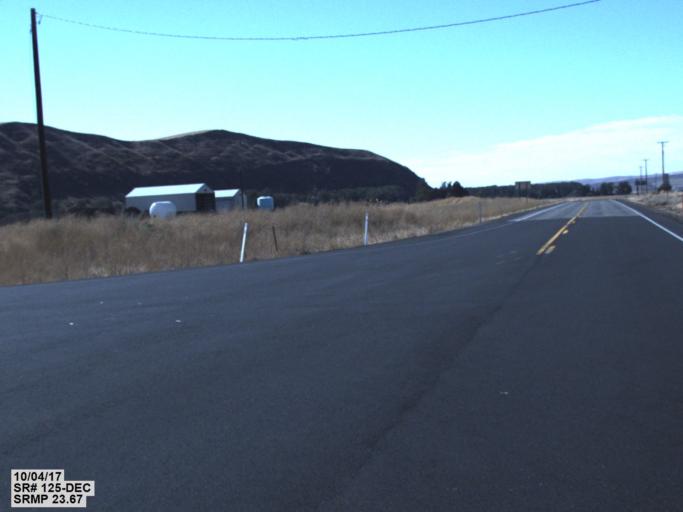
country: US
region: Washington
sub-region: Walla Walla County
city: Waitsburg
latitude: 46.2987
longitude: -118.3410
